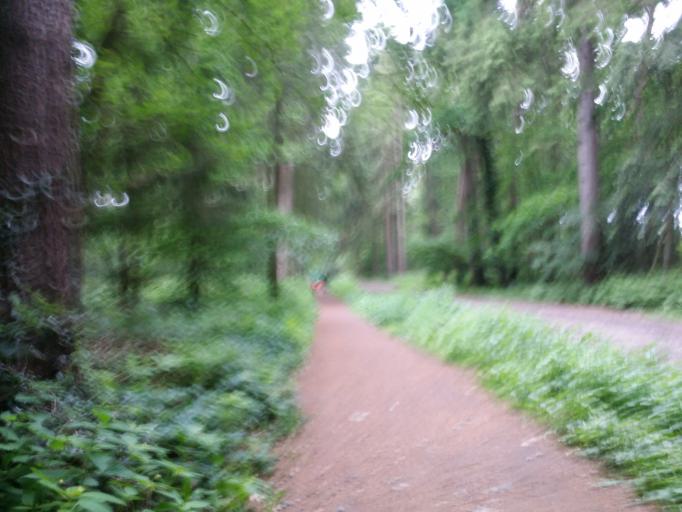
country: DE
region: Lower Saxony
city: Rastede
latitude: 53.2343
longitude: 8.2423
